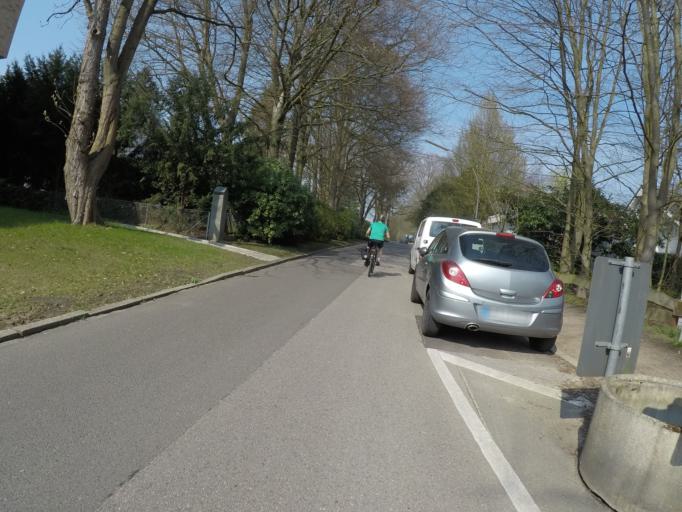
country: DE
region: Hamburg
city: Wohldorf-Ohlstedt
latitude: 53.6859
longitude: 10.1148
